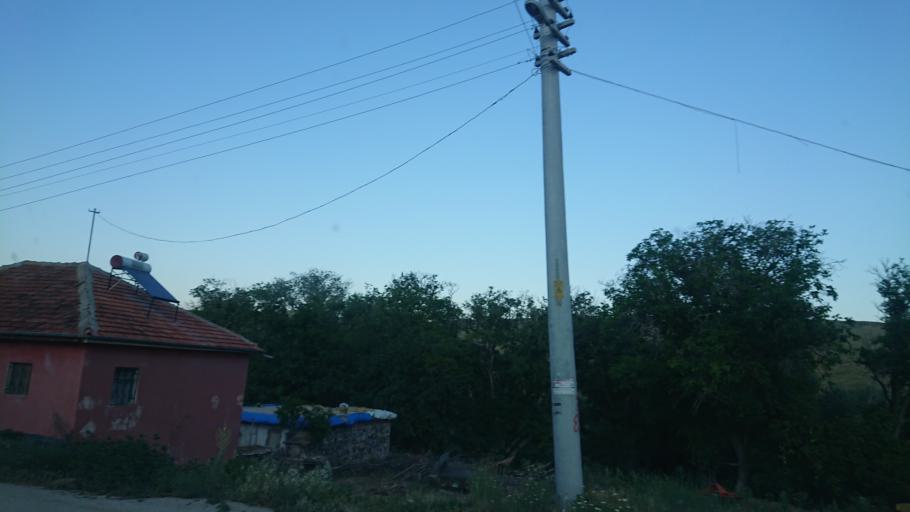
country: TR
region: Aksaray
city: Agacoren
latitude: 38.9037
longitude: 33.8588
